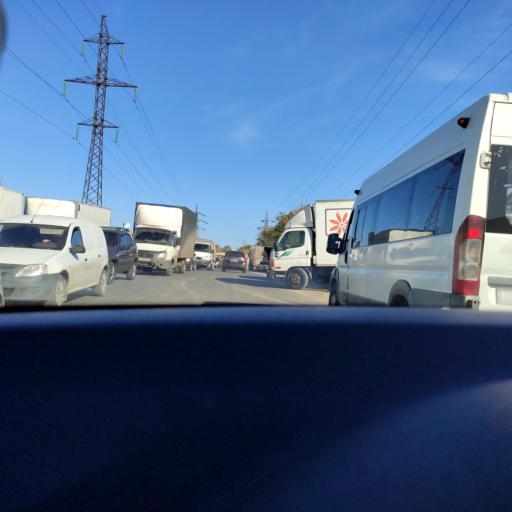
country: RU
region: Samara
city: Petra-Dubrava
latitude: 53.2531
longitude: 50.2948
